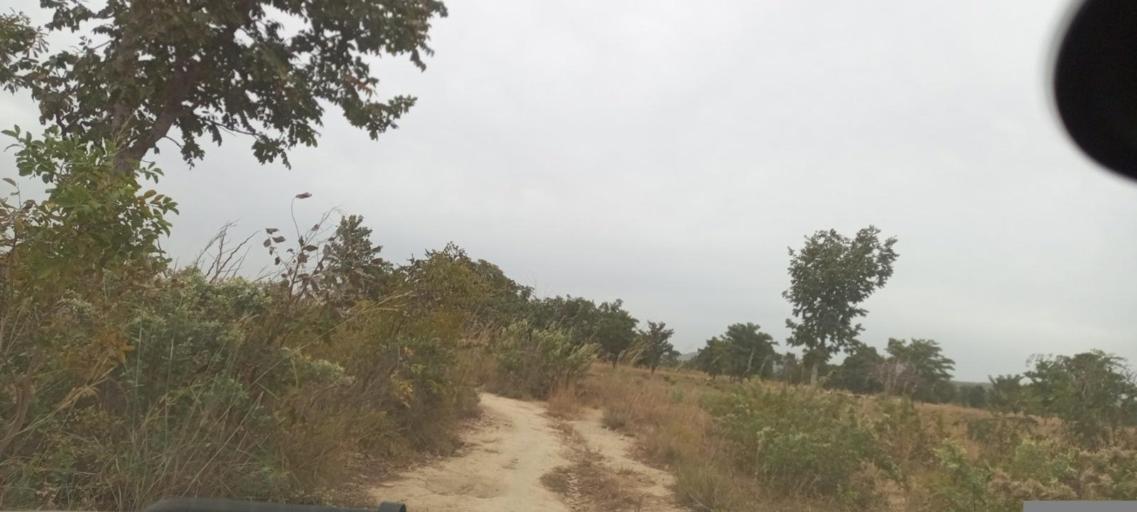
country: ML
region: Koulikoro
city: Kati
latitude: 12.7694
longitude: -8.3798
